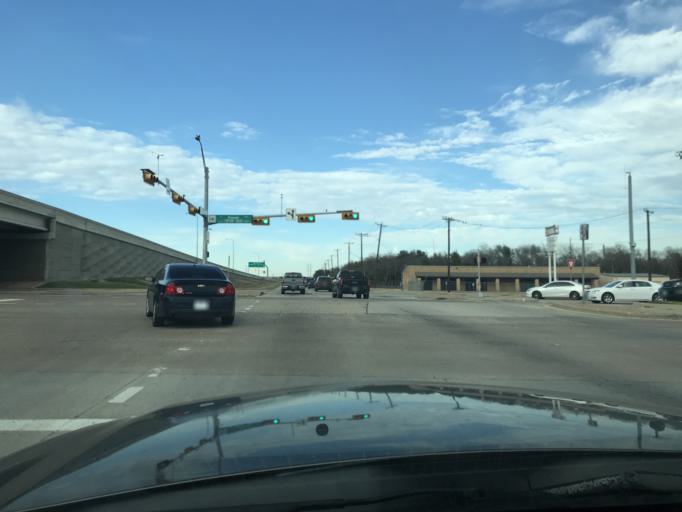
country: US
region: Texas
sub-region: Dallas County
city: Grand Prairie
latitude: 32.7096
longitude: -97.0242
